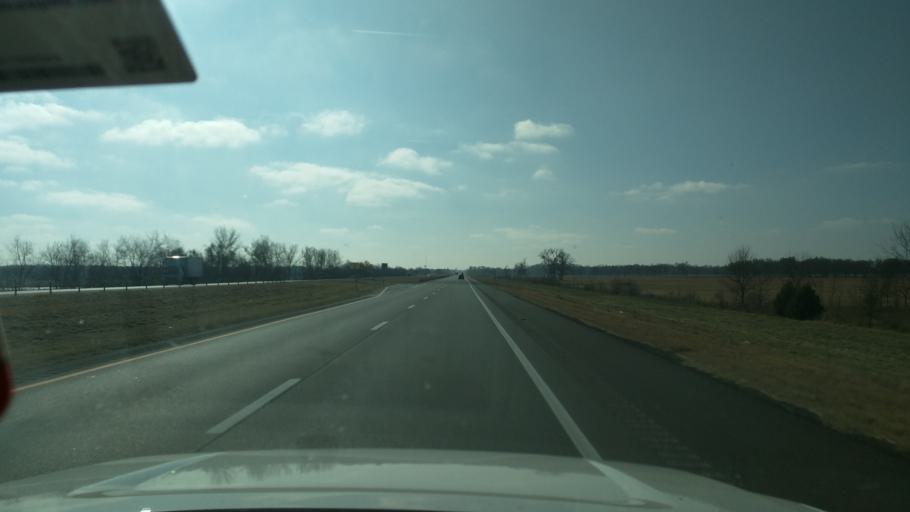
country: US
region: Oklahoma
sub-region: Washington County
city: Bartlesville
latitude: 36.6639
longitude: -95.9356
